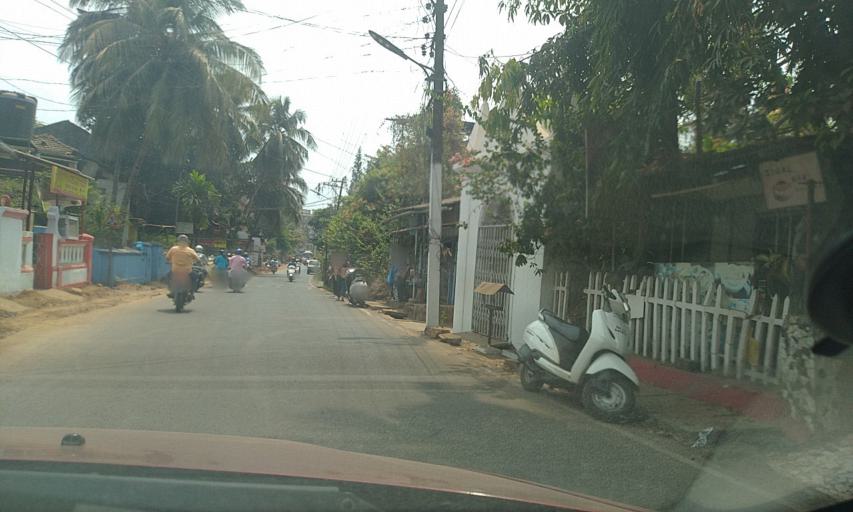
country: IN
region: Goa
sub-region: North Goa
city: Mapuca
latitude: 15.5935
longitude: 73.8045
